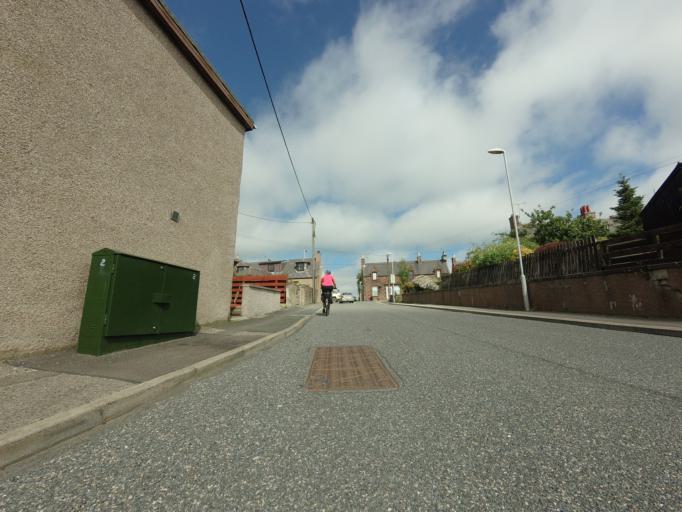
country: GB
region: Scotland
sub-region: Aberdeenshire
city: Turriff
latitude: 57.5388
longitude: -2.4663
